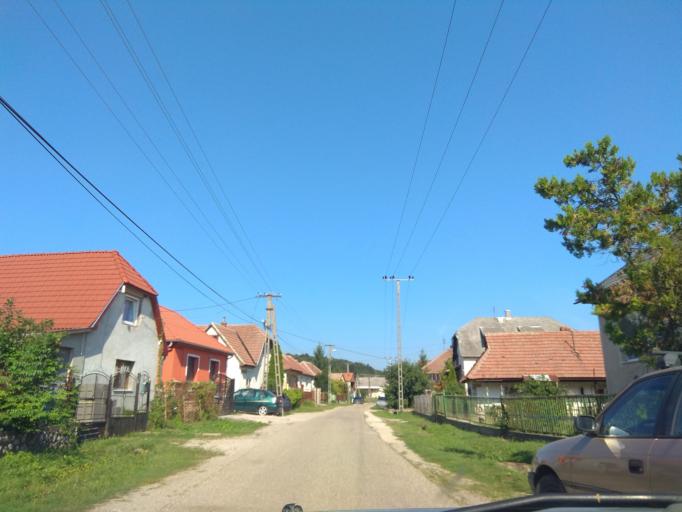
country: HU
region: Borsod-Abauj-Zemplen
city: Harsany
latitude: 47.9837
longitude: 20.7817
